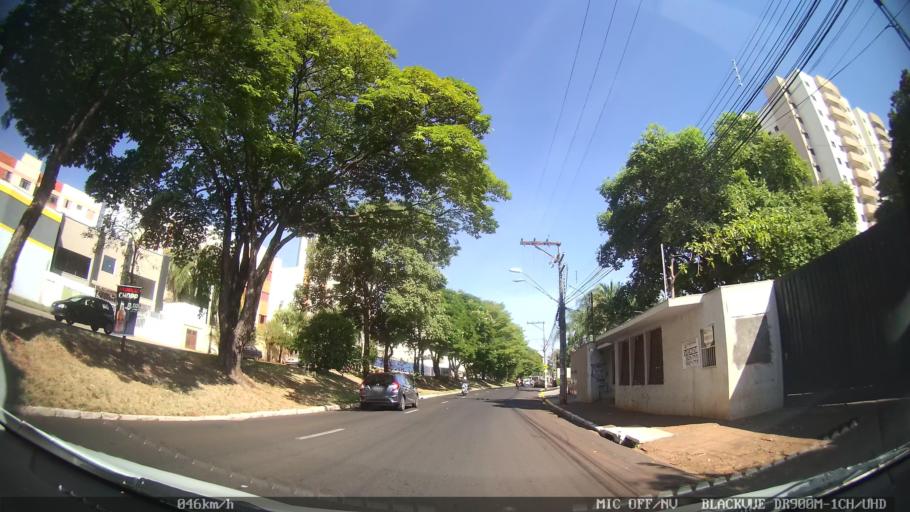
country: BR
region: Sao Paulo
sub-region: Ribeirao Preto
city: Ribeirao Preto
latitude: -21.1894
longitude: -47.8201
